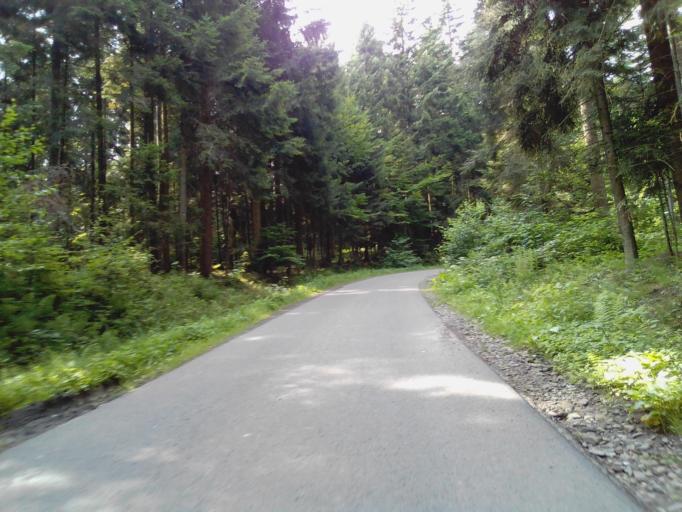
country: PL
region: Subcarpathian Voivodeship
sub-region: Powiat strzyzowski
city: Frysztak
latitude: 49.8591
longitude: 21.5370
